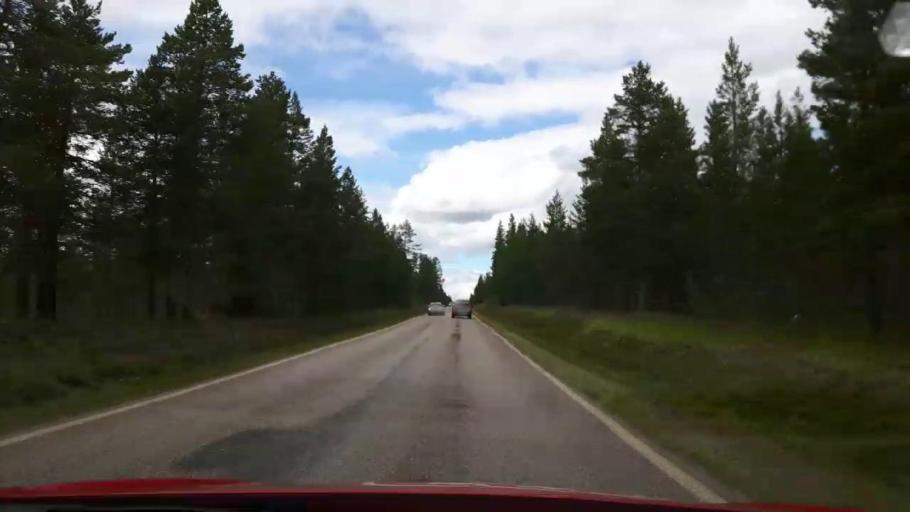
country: NO
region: Hedmark
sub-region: Trysil
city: Innbygda
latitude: 61.8421
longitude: 12.9557
